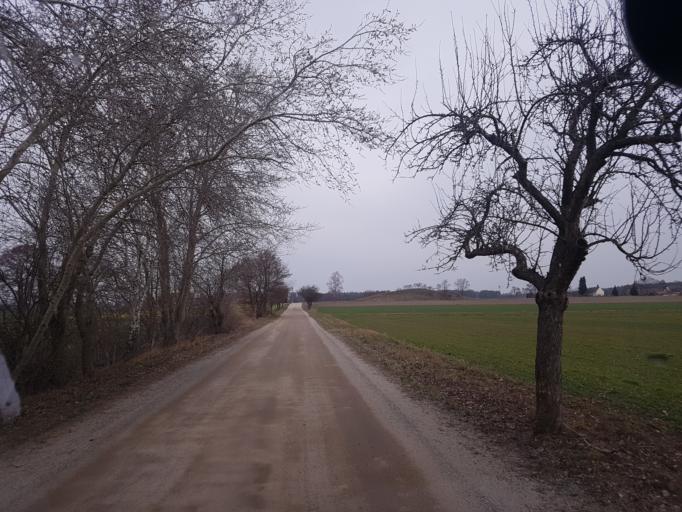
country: DE
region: Brandenburg
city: Finsterwalde
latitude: 51.6598
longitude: 13.6763
